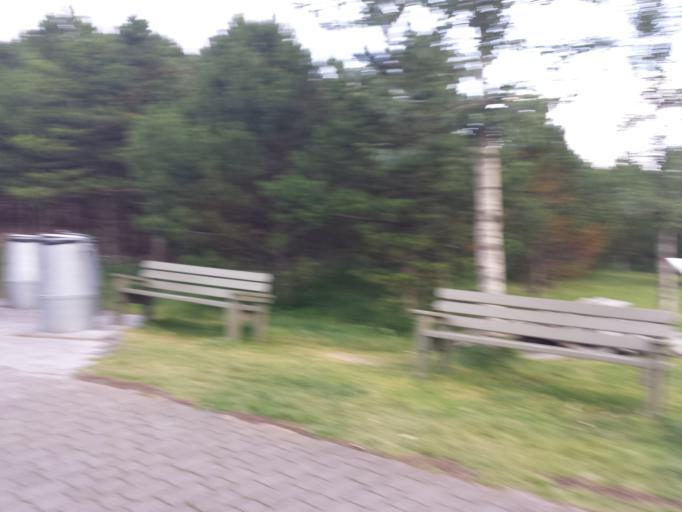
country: IS
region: Capital Region
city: Reykjavik
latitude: 64.0737
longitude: -21.8242
